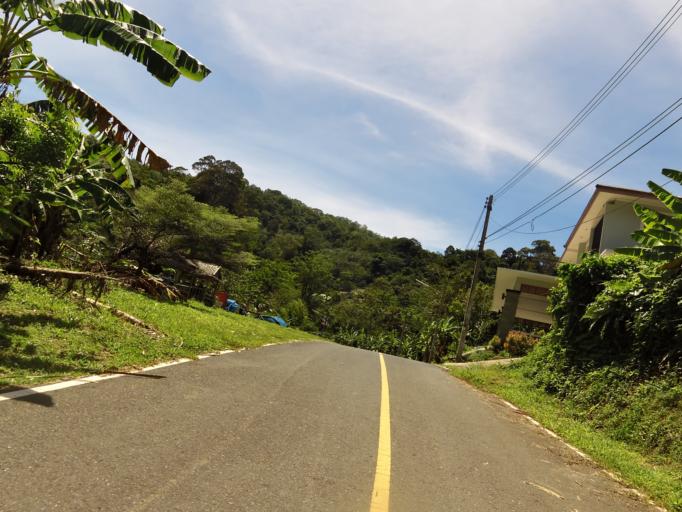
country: TH
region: Phuket
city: Ban Karon
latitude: 7.8462
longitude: 98.3088
